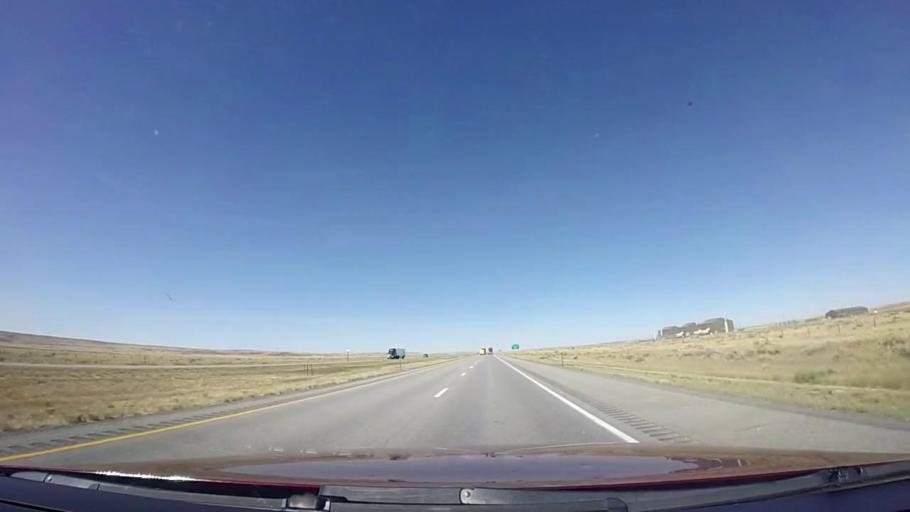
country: US
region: Wyoming
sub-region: Carbon County
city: Rawlins
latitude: 41.6673
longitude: -108.0194
